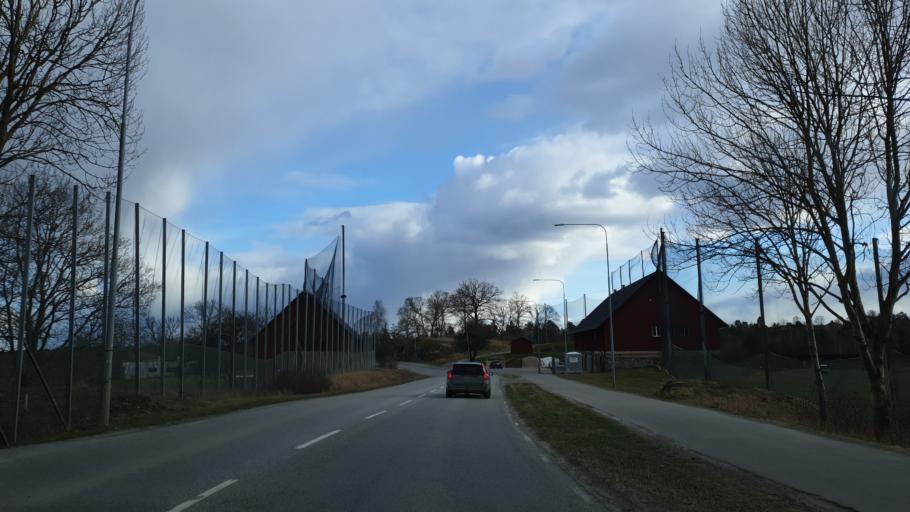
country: SE
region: Stockholm
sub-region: Lidingo
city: Lidingoe
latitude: 59.3786
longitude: 18.1271
